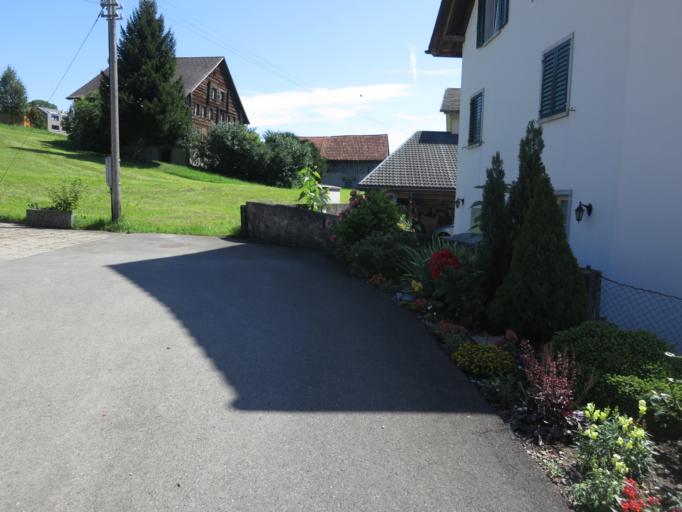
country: CH
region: Schwyz
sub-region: Bezirk March
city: Schubelbach
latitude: 47.1915
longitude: 8.9116
